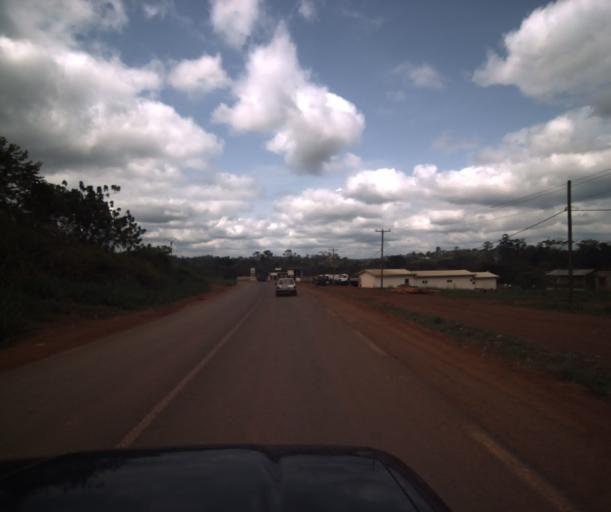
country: CM
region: Centre
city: Yaounde
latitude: 3.7940
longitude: 11.4754
